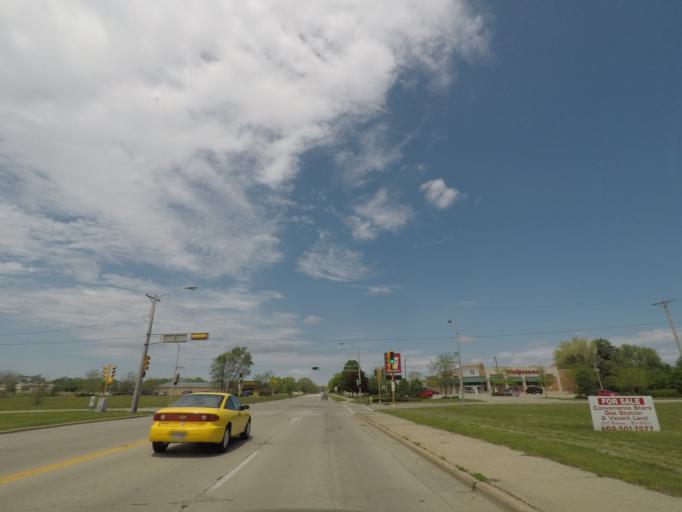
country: US
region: Wisconsin
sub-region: Rock County
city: Beloit
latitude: 42.5183
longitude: -89.0653
